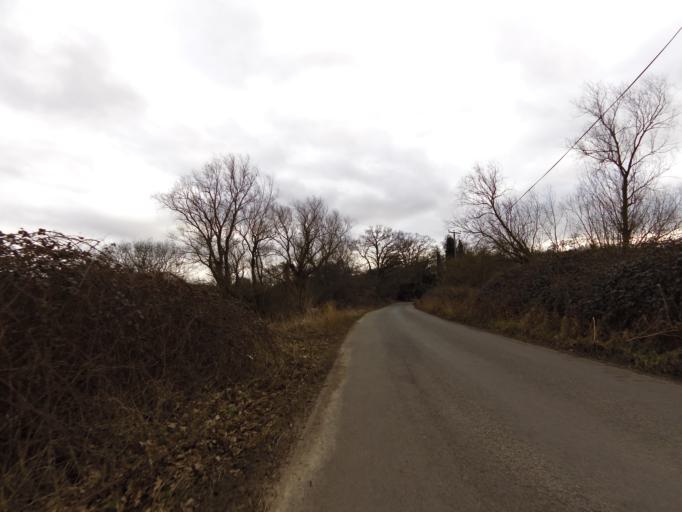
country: GB
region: England
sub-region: Suffolk
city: Woodbridge
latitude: 52.0310
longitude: 1.3081
